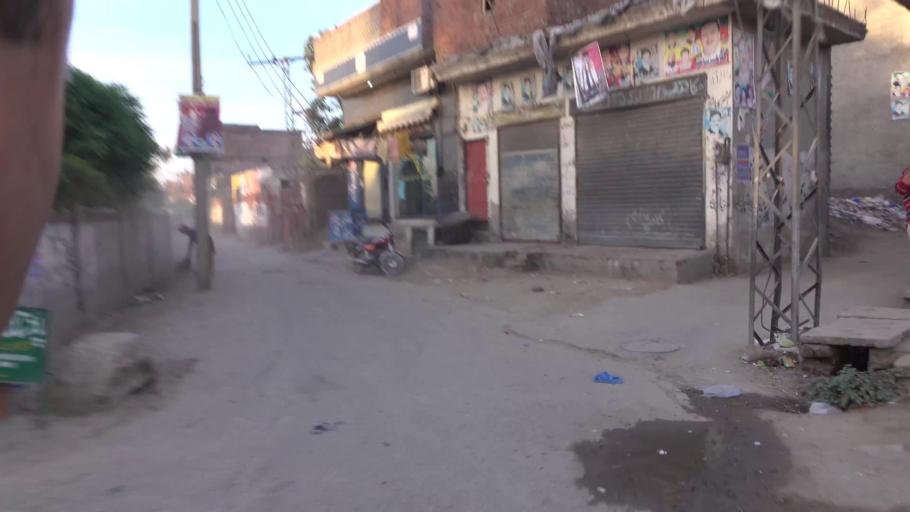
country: PK
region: Punjab
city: Hafizabad
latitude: 32.0663
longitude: 73.6888
